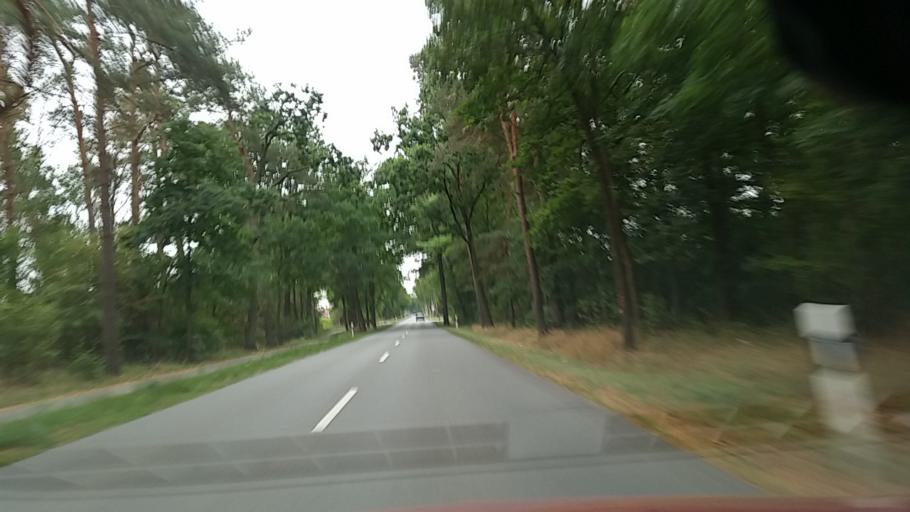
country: DE
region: Lower Saxony
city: Bokensdorf
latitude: 52.5086
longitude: 10.7162
